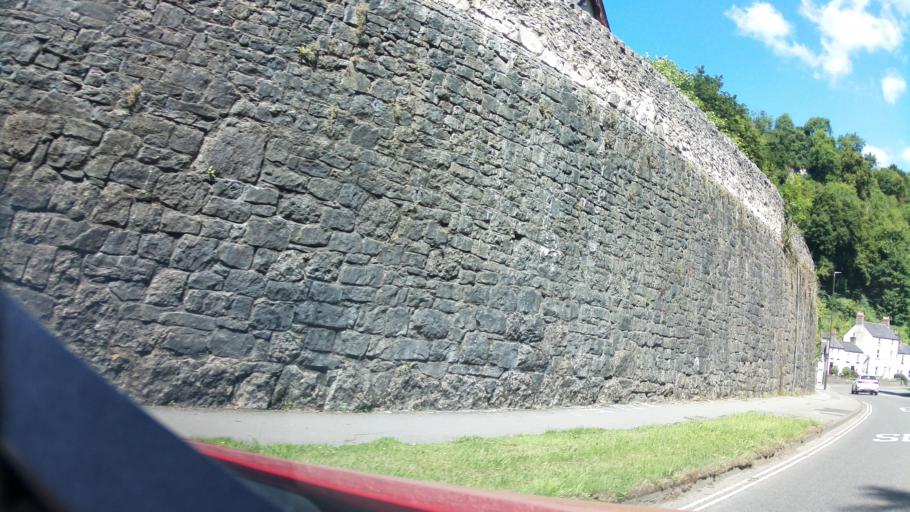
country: GB
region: England
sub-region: Derbyshire
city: Matlock
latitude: 53.1295
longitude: -1.5599
